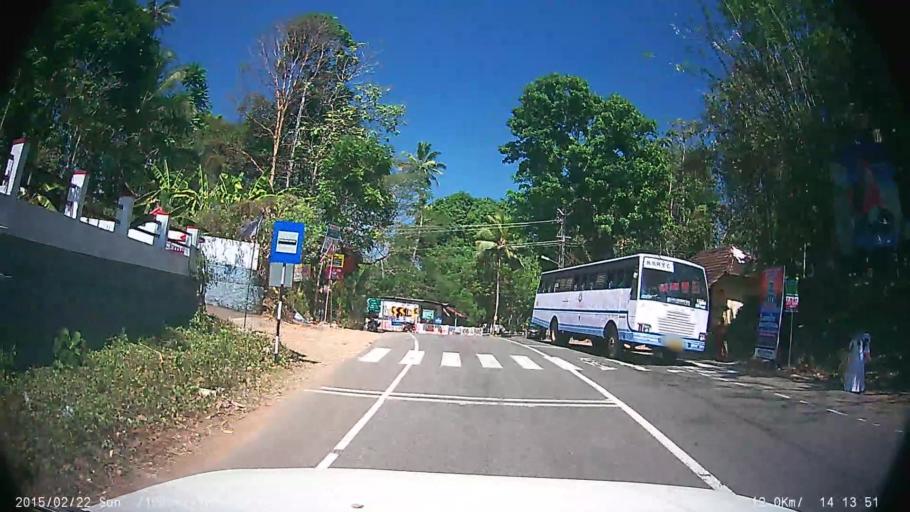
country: IN
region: Kerala
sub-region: Kottayam
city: Kottayam
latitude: 9.5407
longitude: 76.6828
